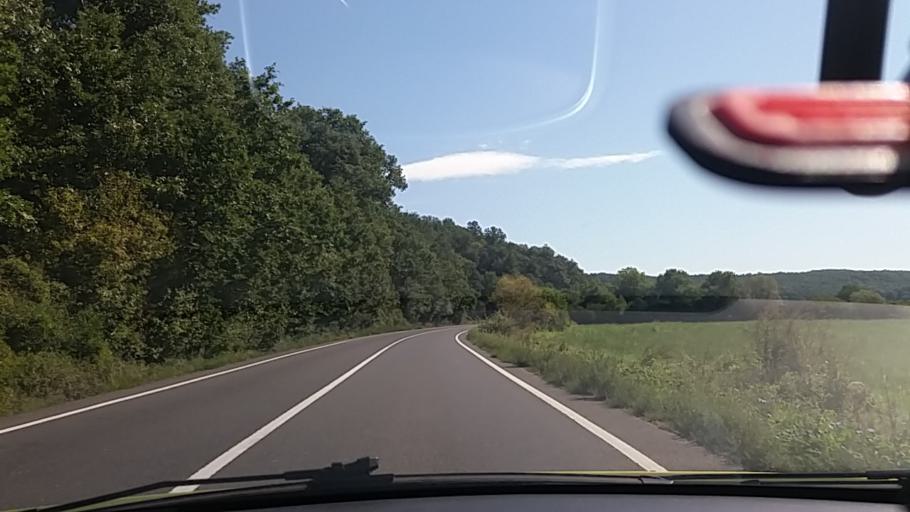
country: RO
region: Arad
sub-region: Comuna Ususau
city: Ususau
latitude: 46.1064
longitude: 21.7766
